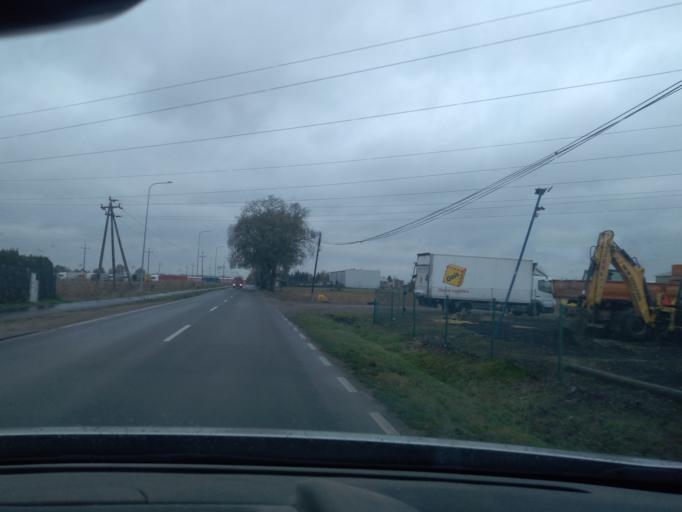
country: PL
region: Greater Poland Voivodeship
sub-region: Powiat obornicki
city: Oborniki
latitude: 52.6483
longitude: 16.8463
